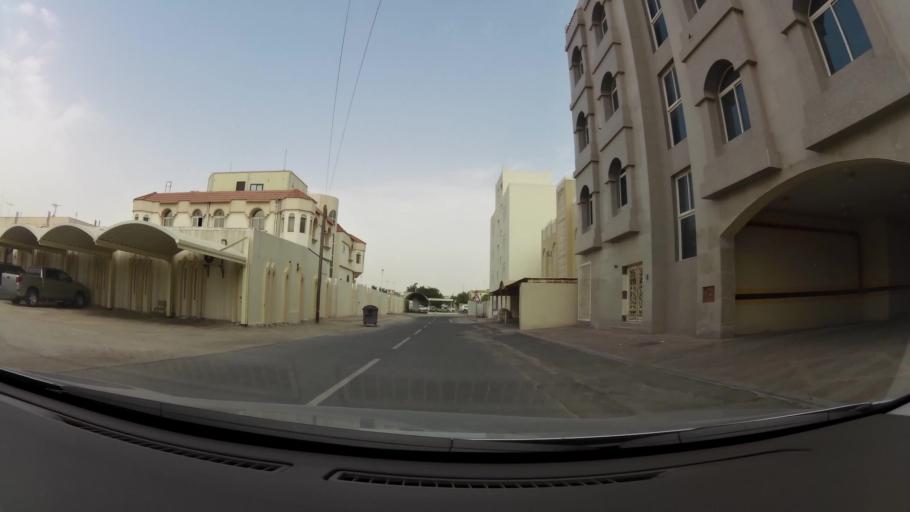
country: QA
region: Baladiyat ad Dawhah
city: Doha
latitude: 25.3088
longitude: 51.4949
